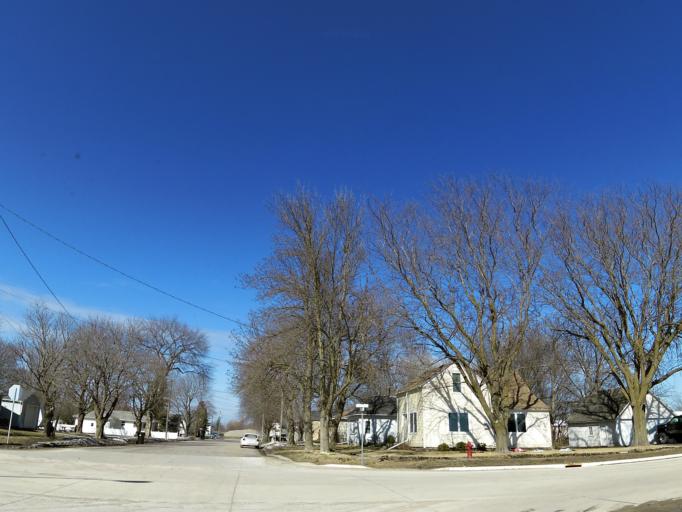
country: US
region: Minnesota
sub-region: Waseca County
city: New Richland
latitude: 43.8970
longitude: -93.4938
